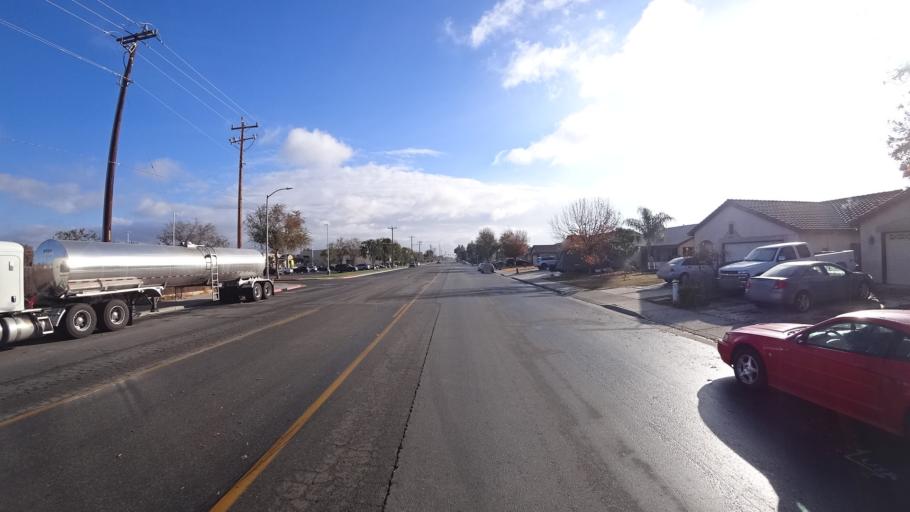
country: US
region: California
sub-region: Kern County
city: Greenfield
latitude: 35.2886
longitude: -119.0078
